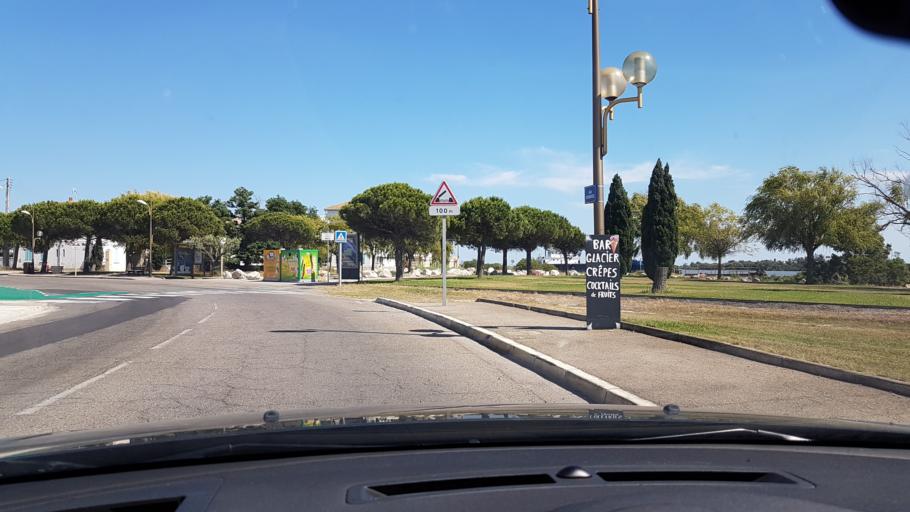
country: FR
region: Provence-Alpes-Cote d'Azur
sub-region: Departement des Bouches-du-Rhone
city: Port-Saint-Louis-du-Rhone
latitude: 43.3836
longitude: 4.8065
